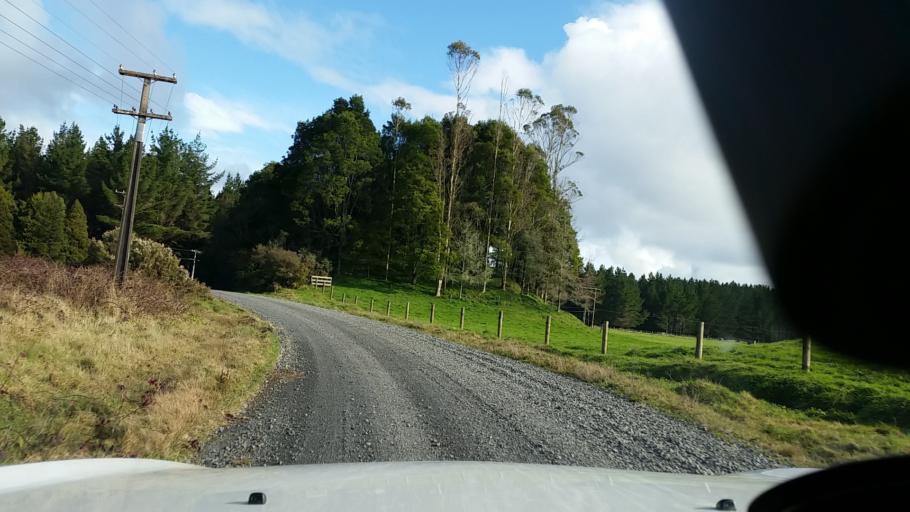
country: NZ
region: Bay of Plenty
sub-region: Rotorua District
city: Rotorua
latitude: -38.0812
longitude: 176.0474
